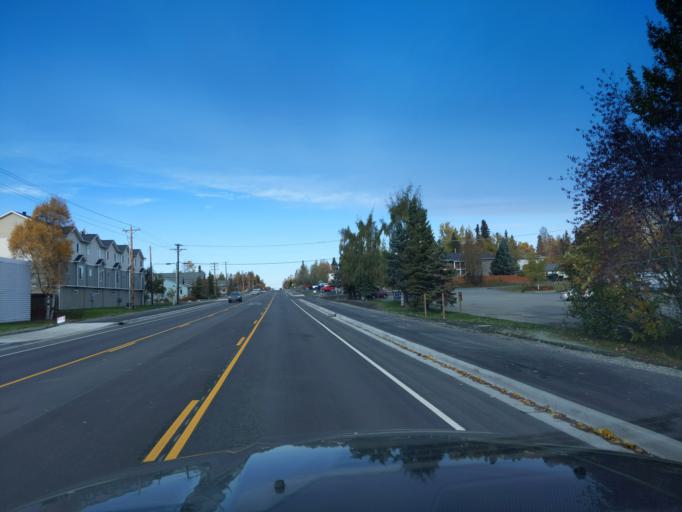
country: US
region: Alaska
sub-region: Anchorage Municipality
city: Anchorage
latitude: 61.1436
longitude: -149.9518
